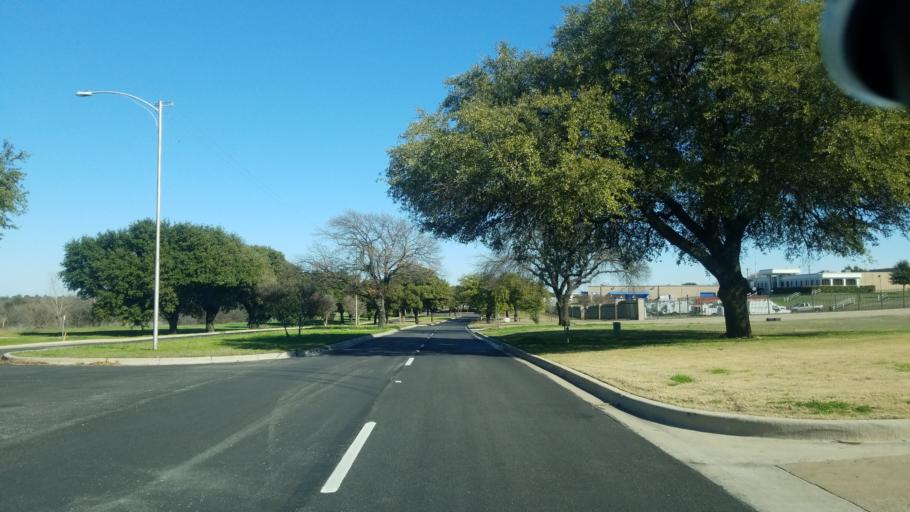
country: US
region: Texas
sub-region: Dallas County
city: Grand Prairie
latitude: 32.7663
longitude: -97.0514
